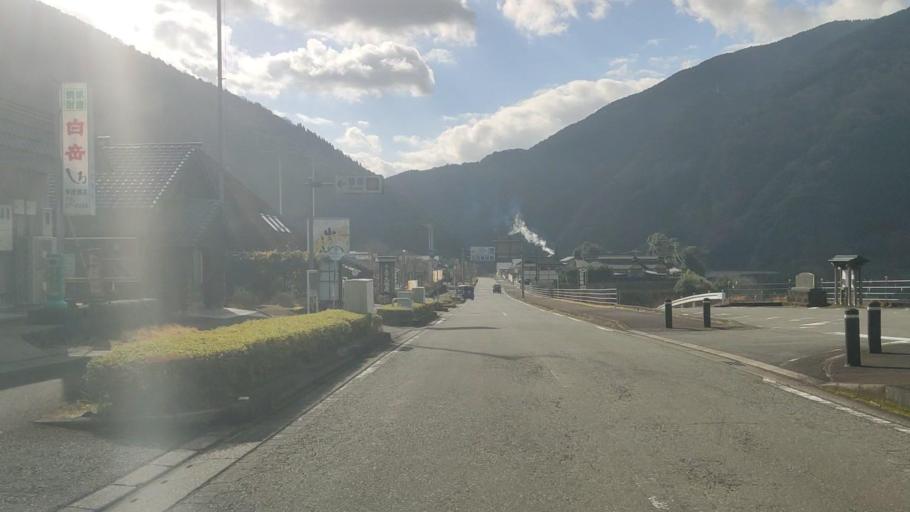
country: JP
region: Kumamoto
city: Hitoyoshi
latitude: 32.3996
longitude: 130.8265
